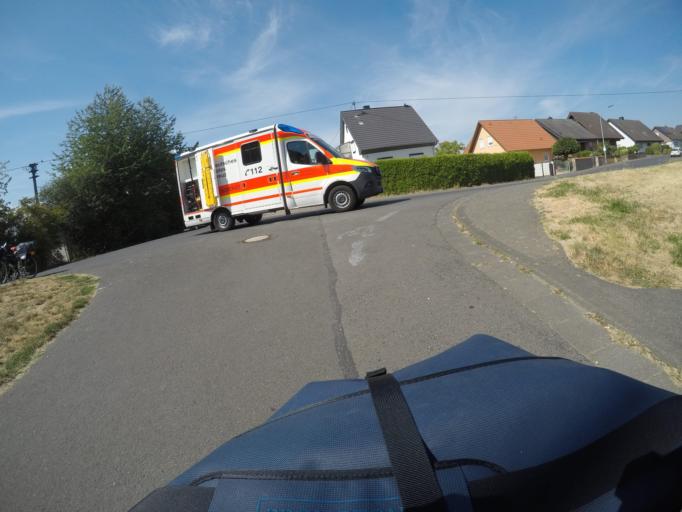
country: DE
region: Rheinland-Pfalz
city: Sinzig
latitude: 50.5485
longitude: 7.2694
